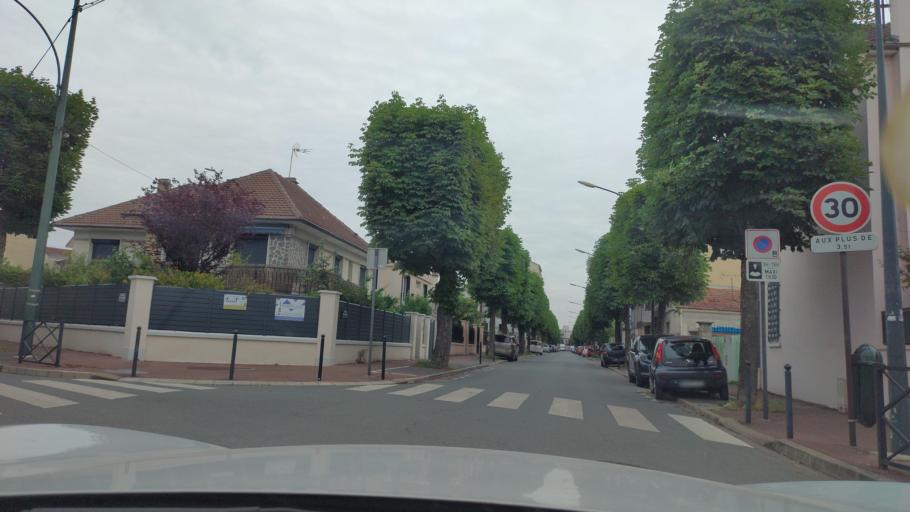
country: FR
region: Ile-de-France
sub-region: Departement du Val-de-Marne
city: Saint-Maur-des-Fosses
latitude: 48.8026
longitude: 2.5116
